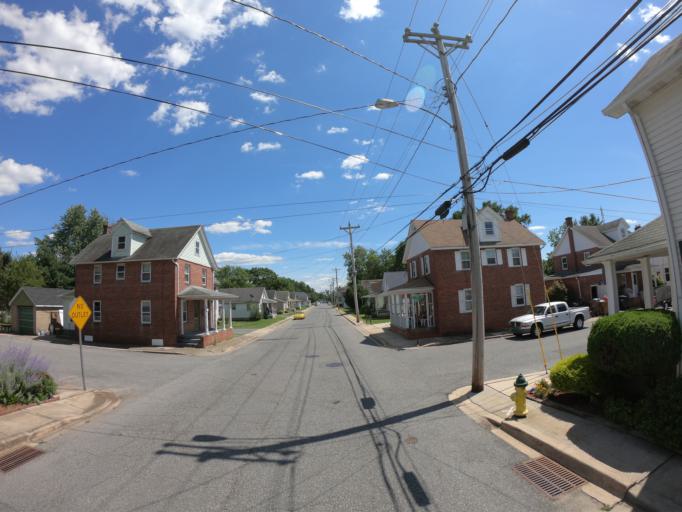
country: US
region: Delaware
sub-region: Sussex County
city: Milford
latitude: 38.9201
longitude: -75.4277
